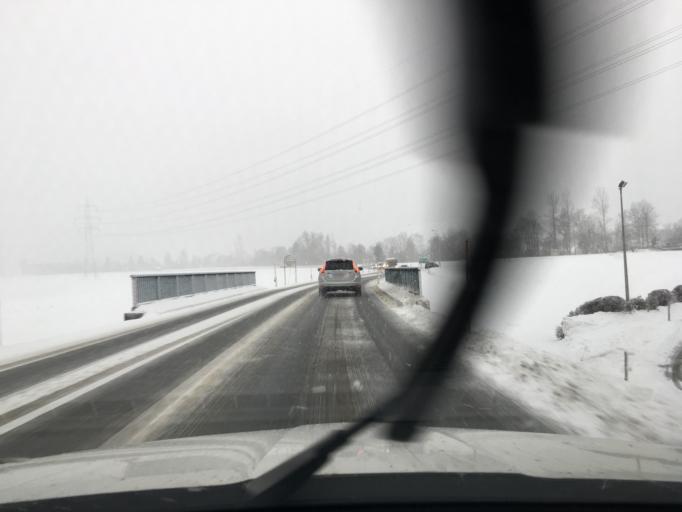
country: AT
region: Tyrol
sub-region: Politischer Bezirk Schwaz
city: Schwendau
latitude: 47.1905
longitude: 11.8691
